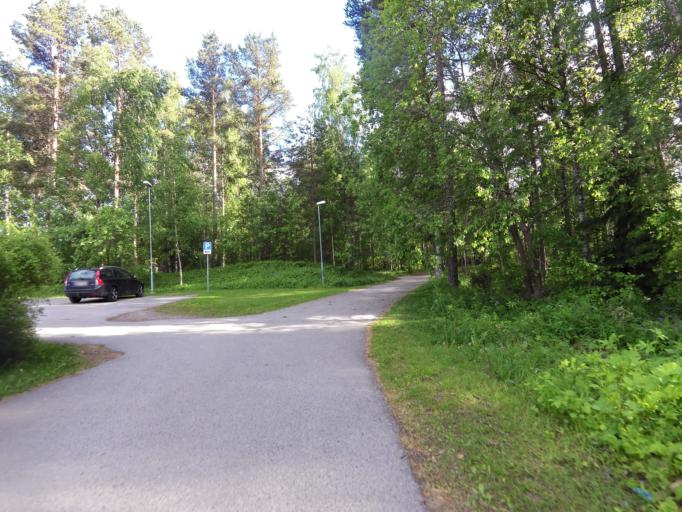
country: SE
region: Gaevleborg
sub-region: Gavle Kommun
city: Gavle
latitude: 60.6906
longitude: 17.0989
